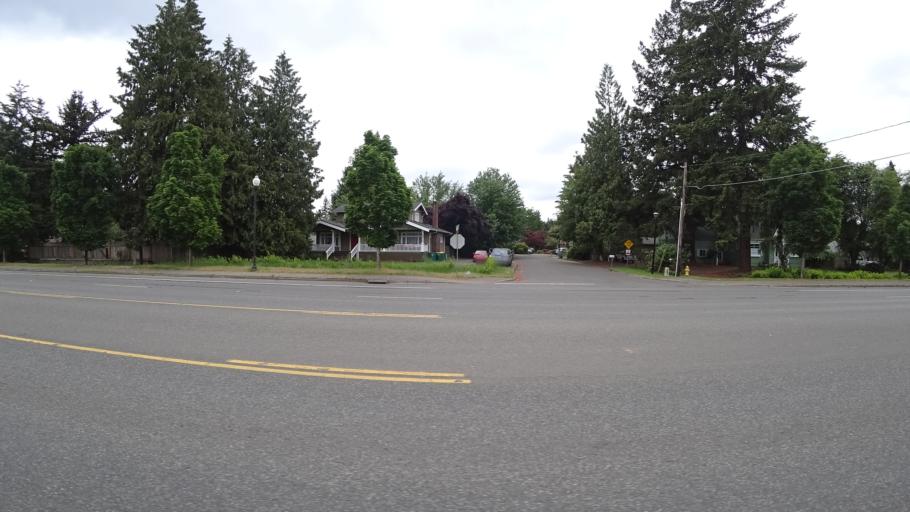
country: US
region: Oregon
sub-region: Washington County
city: Aloha
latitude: 45.4842
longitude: -122.8398
